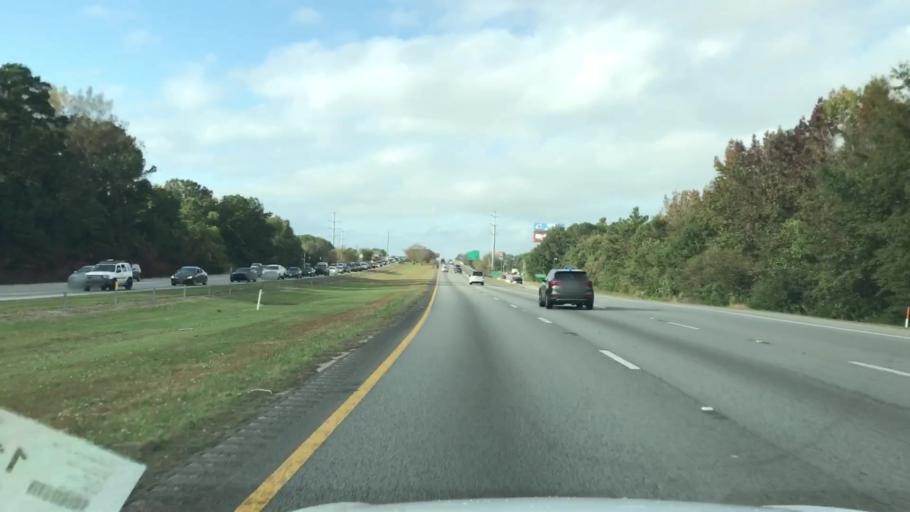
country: US
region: South Carolina
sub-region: Charleston County
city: North Charleston
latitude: 32.8494
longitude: -80.0184
